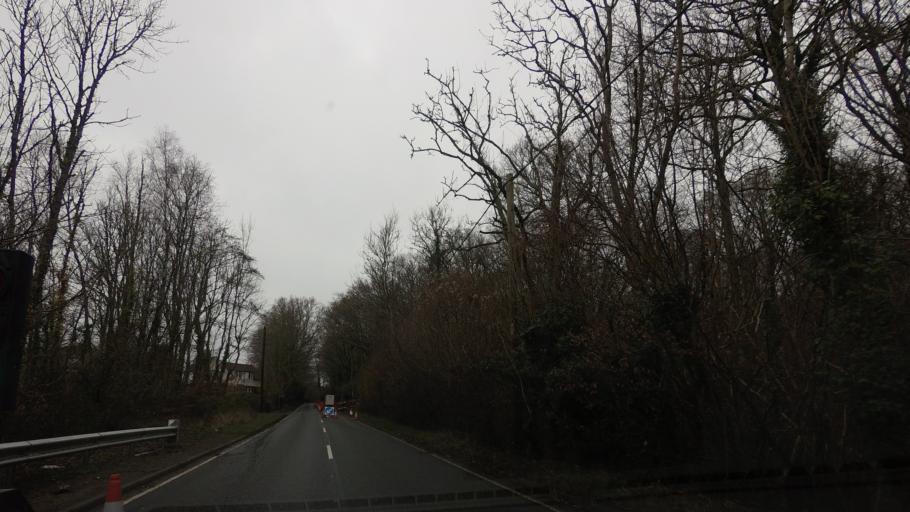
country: GB
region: England
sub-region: East Sussex
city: Robertsbridge
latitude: 50.9664
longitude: 0.5261
